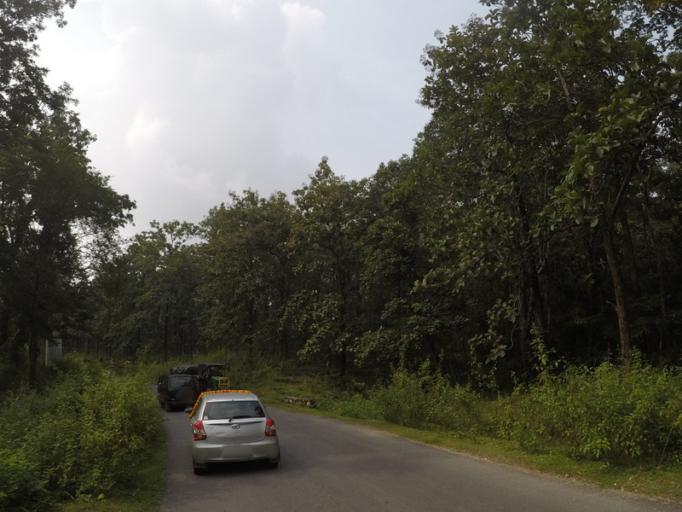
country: IN
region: Karnataka
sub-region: Chikmagalur
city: Mudigere
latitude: 13.2864
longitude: 75.4810
